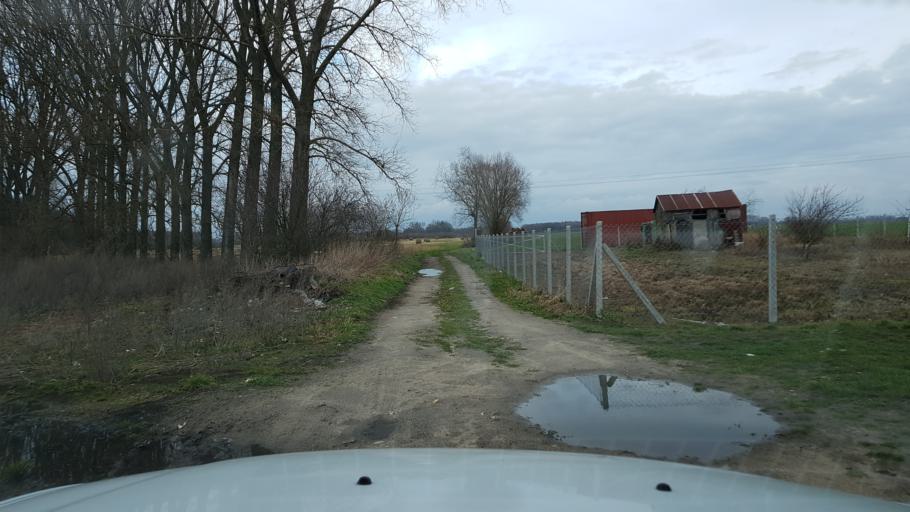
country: PL
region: West Pomeranian Voivodeship
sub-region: Powiat pyrzycki
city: Lipiany
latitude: 52.9969
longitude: 15.0492
